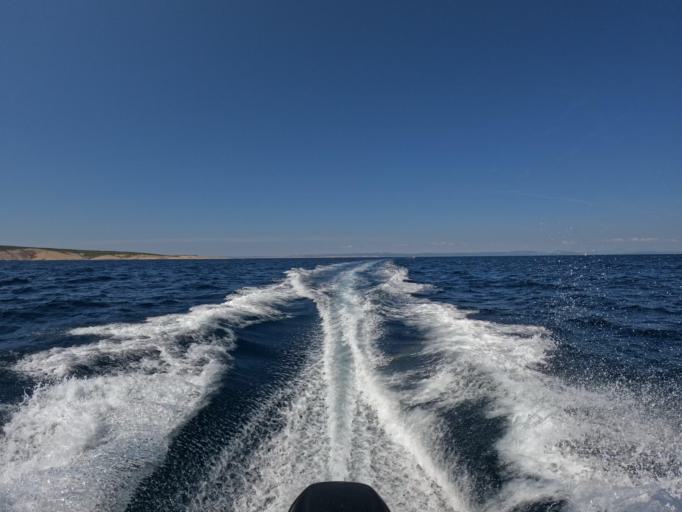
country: HR
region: Primorsko-Goranska
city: Lopar
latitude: 44.8540
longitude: 14.7120
